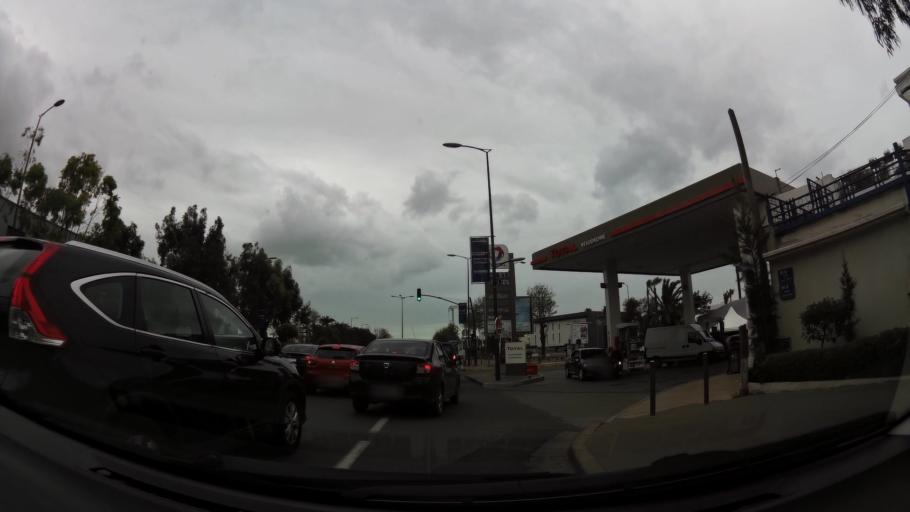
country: MA
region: Grand Casablanca
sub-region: Casablanca
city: Casablanca
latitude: 33.5893
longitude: -7.6487
